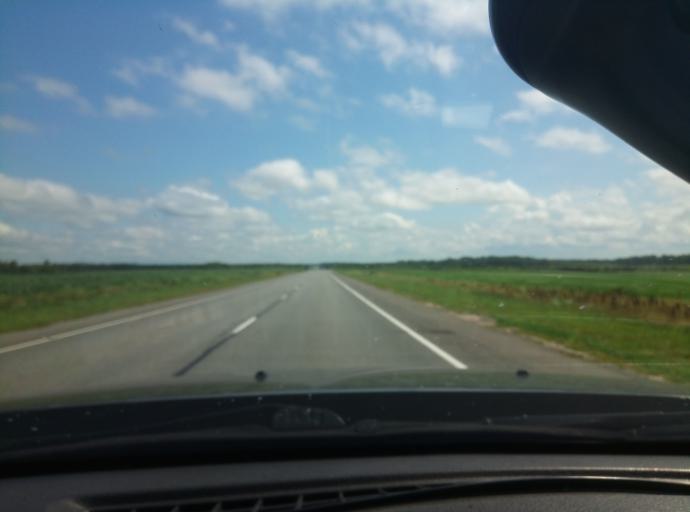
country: RU
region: Tula
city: Khanino
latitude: 54.4052
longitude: 36.5654
